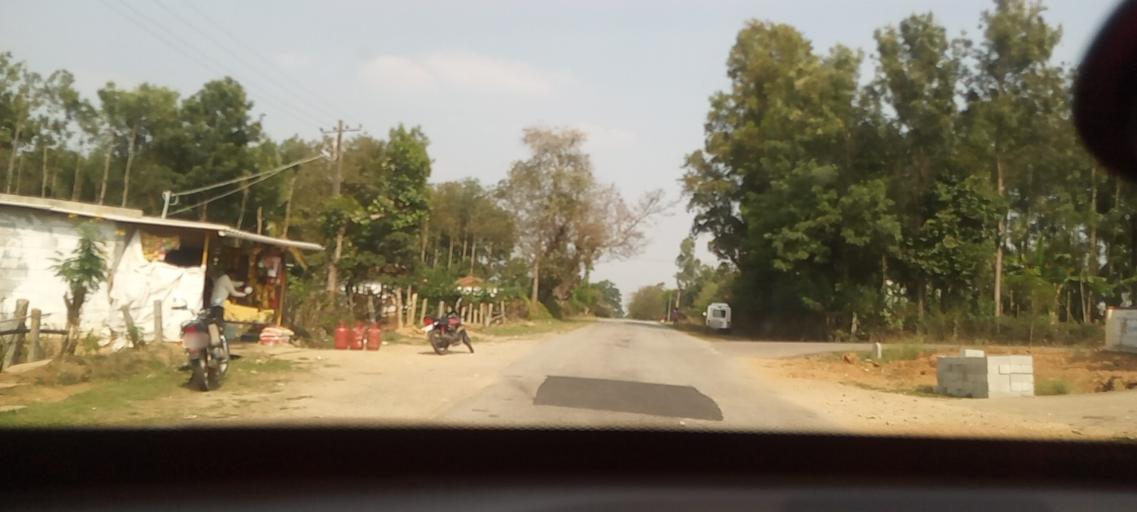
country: IN
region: Karnataka
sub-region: Hassan
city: Belur
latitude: 13.1745
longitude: 75.8144
